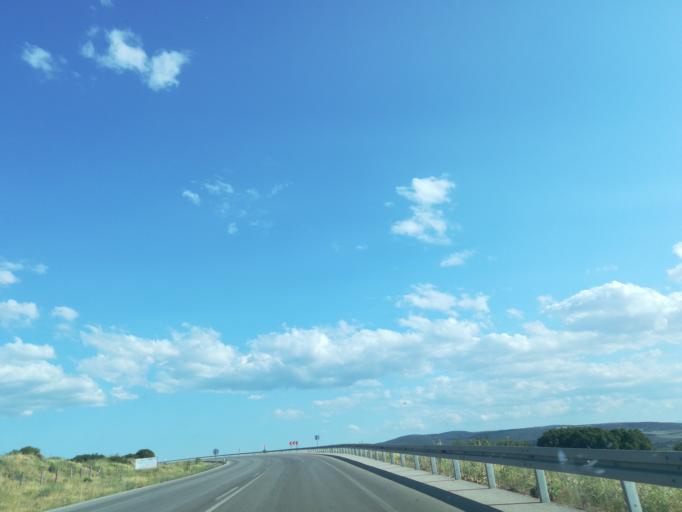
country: TR
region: Denizli
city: Ishakli
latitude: 38.1687
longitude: 30.0712
